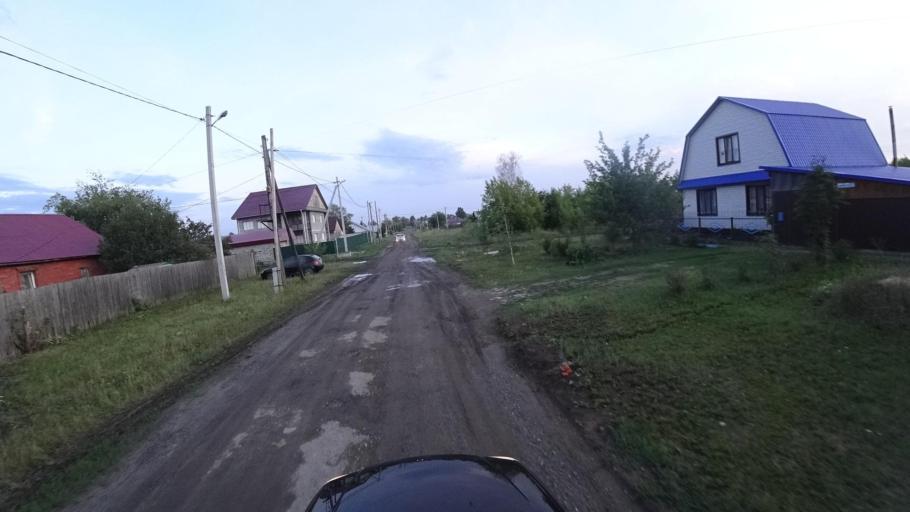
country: RU
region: Sverdlovsk
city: Kamyshlov
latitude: 56.8549
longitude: 62.7338
